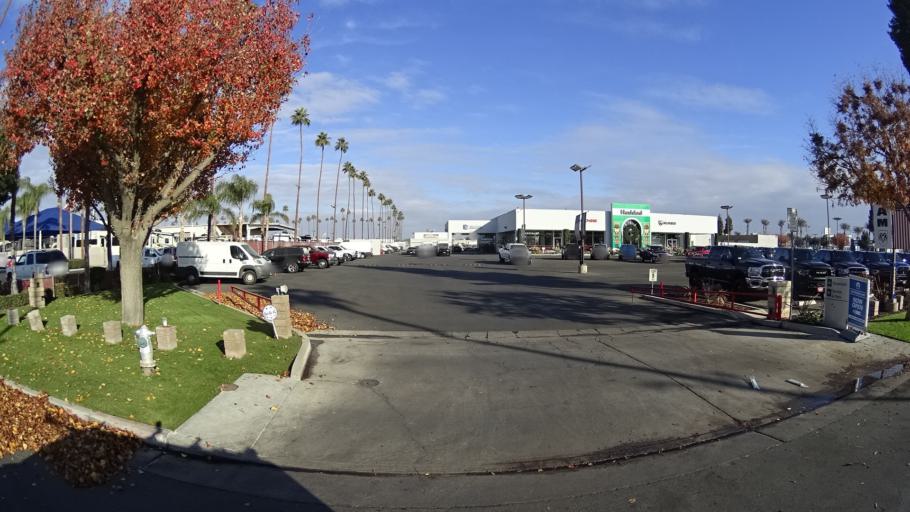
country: US
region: California
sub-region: Kern County
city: Greenfield
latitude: 35.3031
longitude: -119.0370
